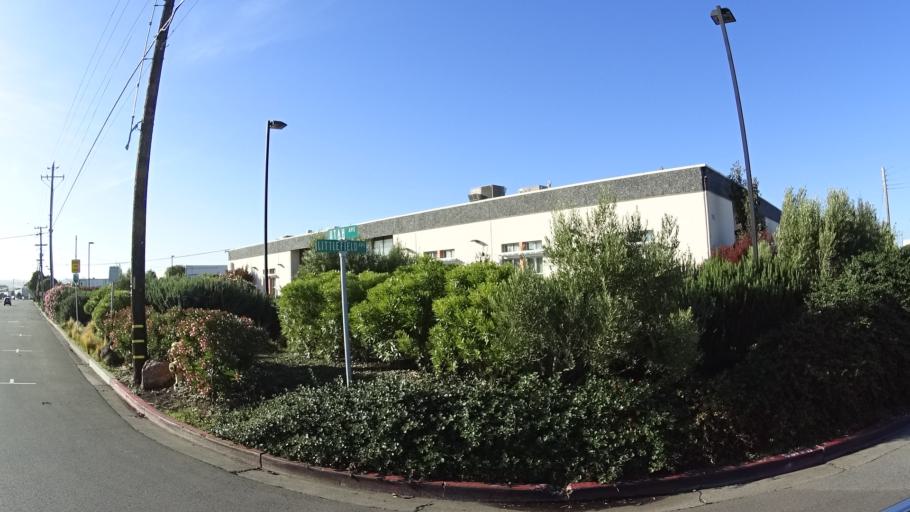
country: US
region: California
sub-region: San Mateo County
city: South San Francisco
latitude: 37.6472
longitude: -122.3945
